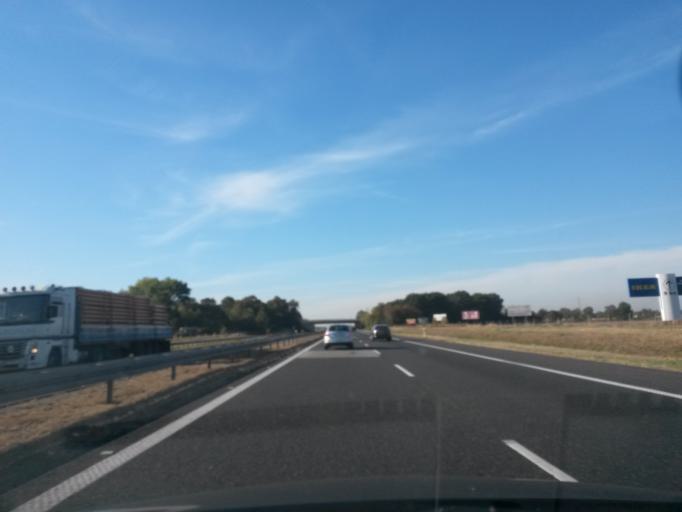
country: PL
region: Lower Silesian Voivodeship
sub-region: Powiat wroclawski
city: Zorawina
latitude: 50.9989
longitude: 17.0420
